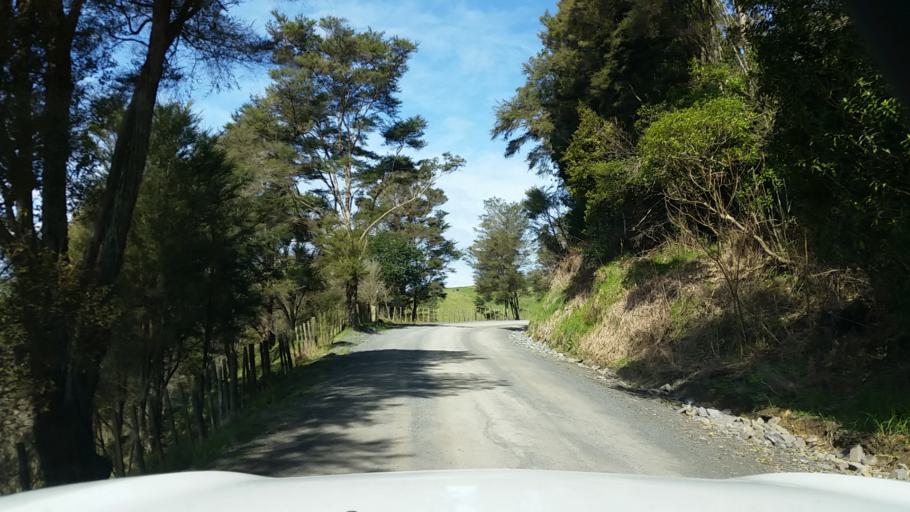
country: NZ
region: Waikato
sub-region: Hauraki District
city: Ngatea
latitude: -37.4464
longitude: 175.4851
